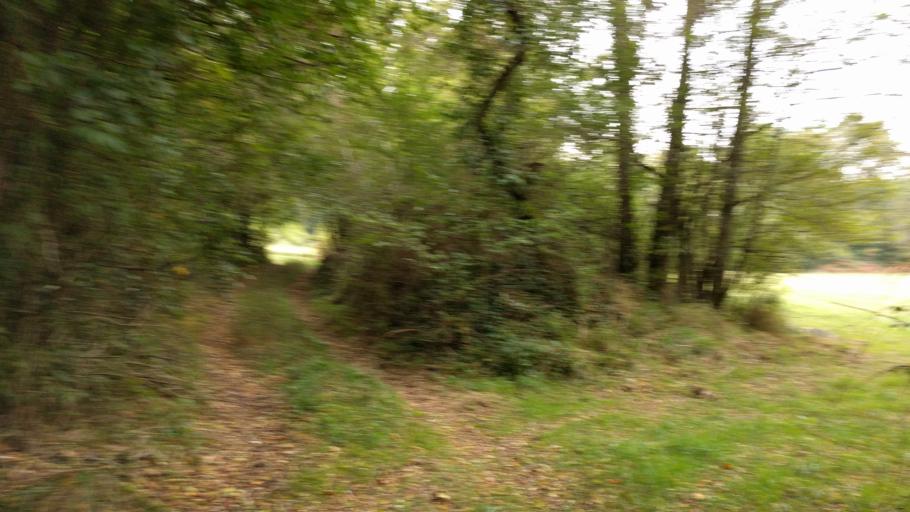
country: FR
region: Aquitaine
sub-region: Departement de la Dordogne
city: Mouleydier
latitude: 44.8948
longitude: 0.6545
